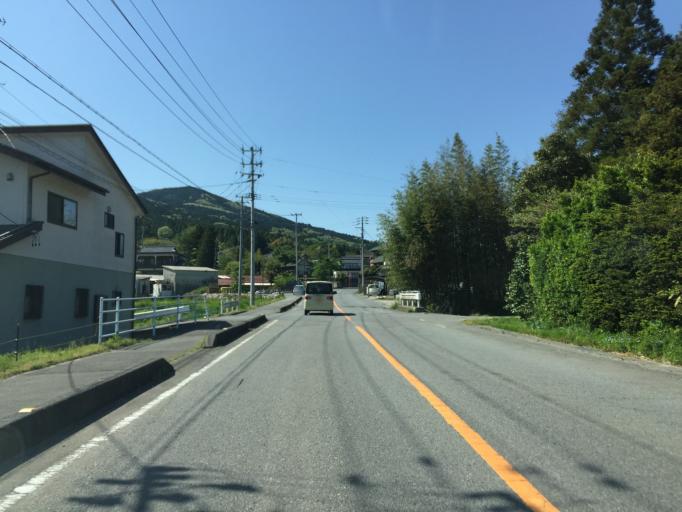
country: JP
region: Fukushima
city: Iwaki
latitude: 37.0471
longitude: 140.7979
